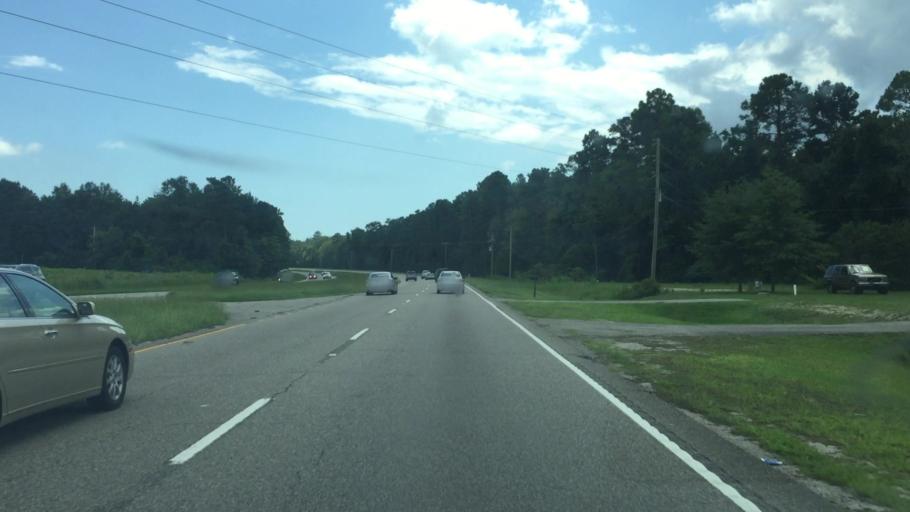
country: US
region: South Carolina
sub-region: Horry County
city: North Myrtle Beach
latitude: 33.9236
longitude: -78.7259
